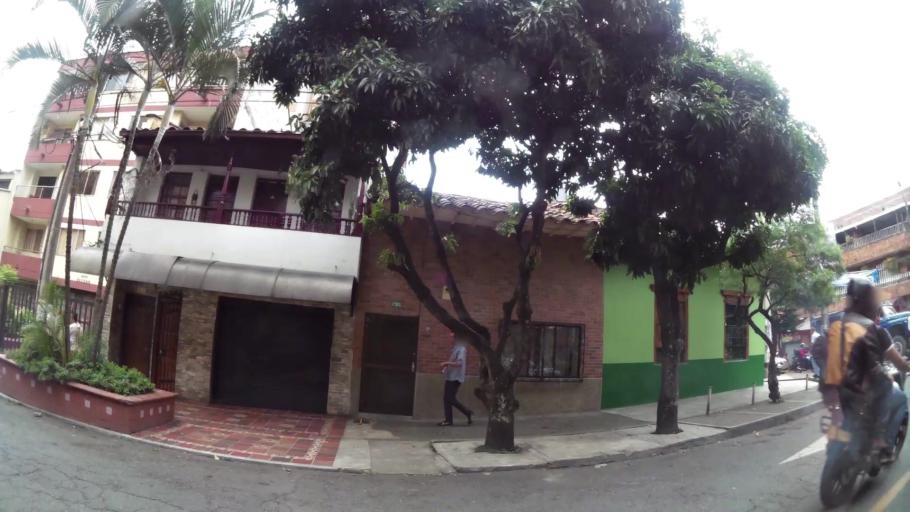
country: CO
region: Antioquia
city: Medellin
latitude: 6.2477
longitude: -75.5565
